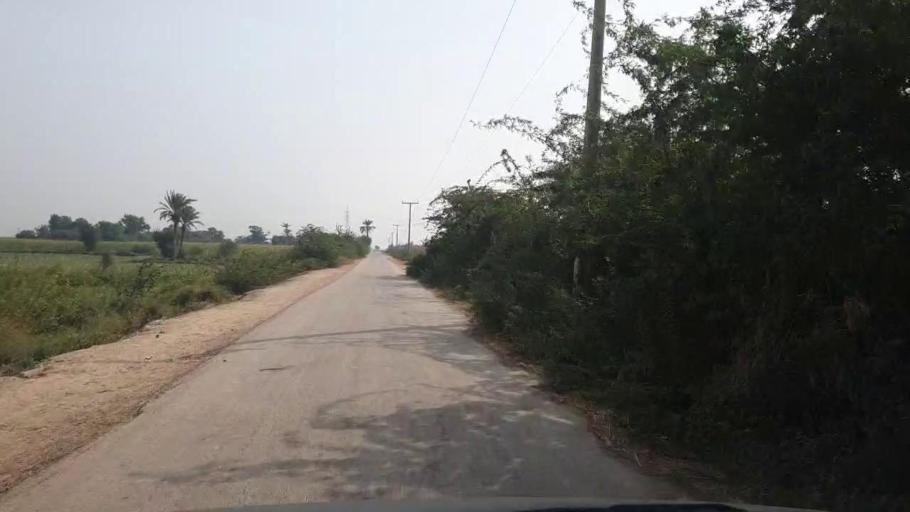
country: PK
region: Sindh
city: Tando Muhammad Khan
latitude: 25.1093
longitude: 68.3646
